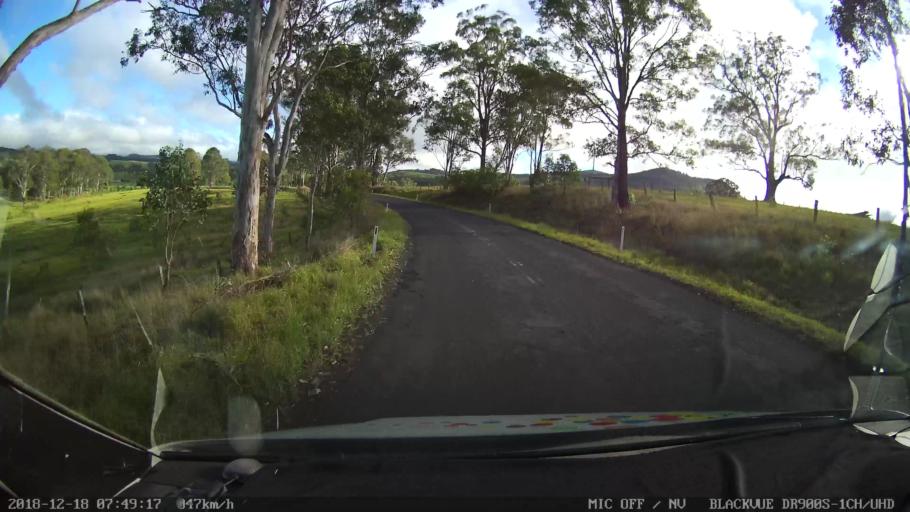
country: AU
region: New South Wales
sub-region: Kyogle
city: Kyogle
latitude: -28.4550
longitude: 152.5699
